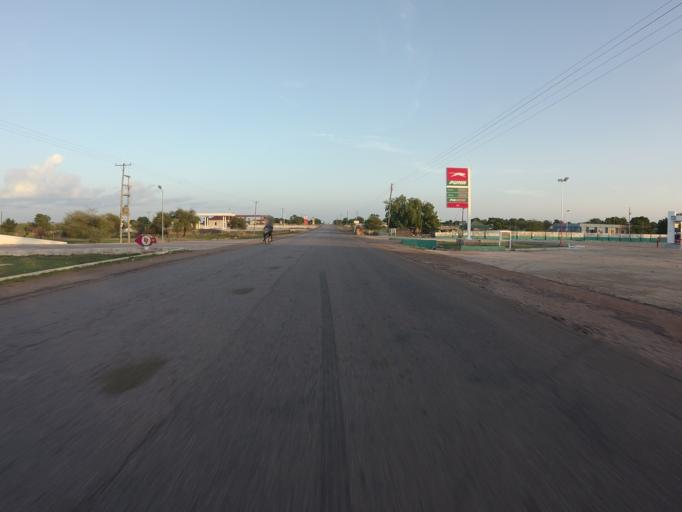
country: GH
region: Upper East
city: Navrongo
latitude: 10.9532
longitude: -1.0963
